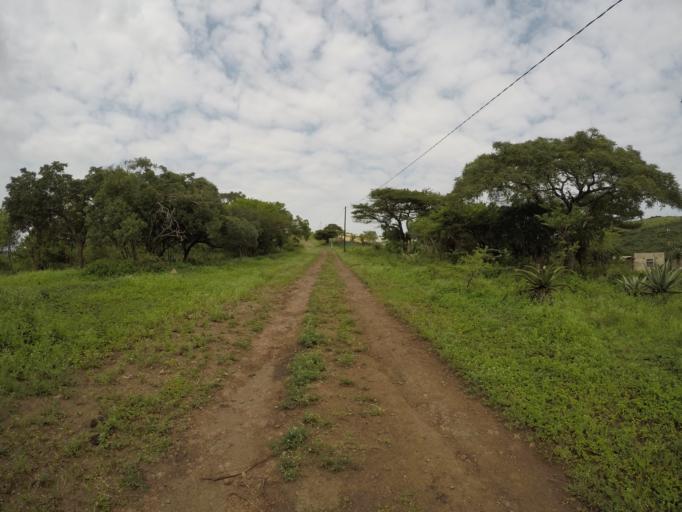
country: ZA
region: KwaZulu-Natal
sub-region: uThungulu District Municipality
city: Empangeni
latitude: -28.6263
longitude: 31.9104
